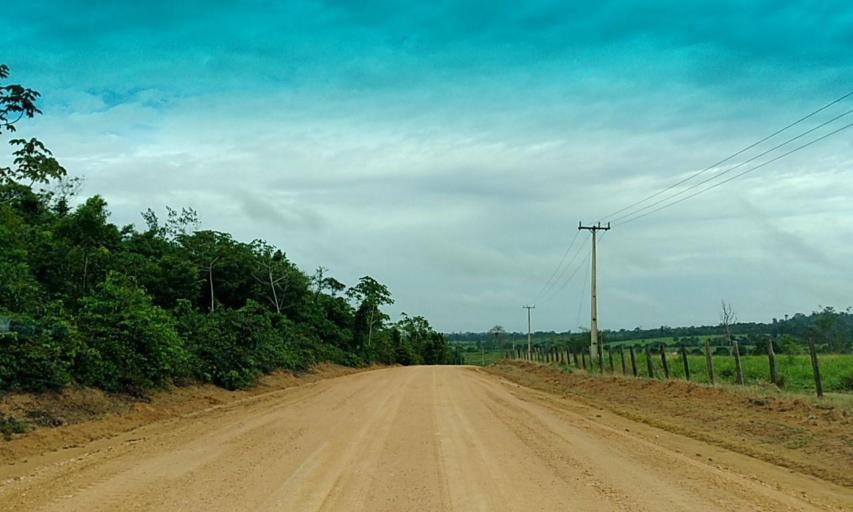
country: BR
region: Para
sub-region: Senador Jose Porfirio
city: Senador Jose Porfirio
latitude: -3.0467
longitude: -51.6782
